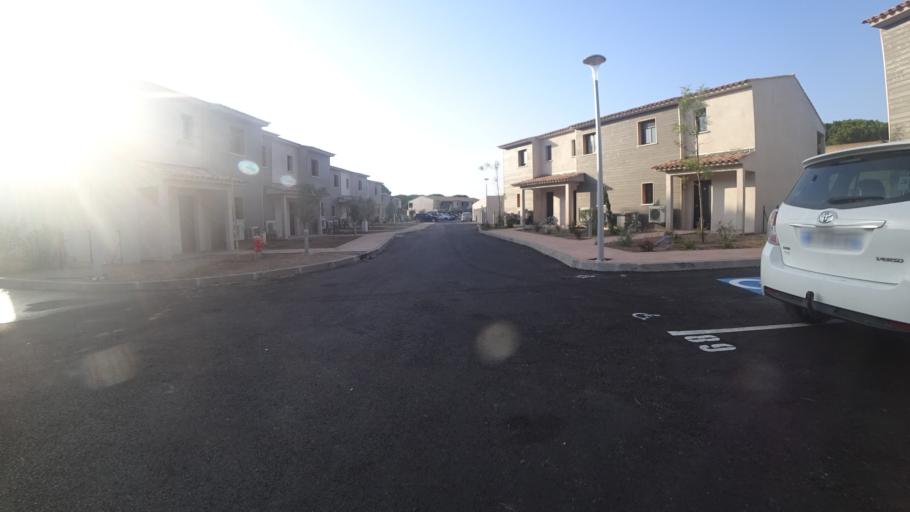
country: FR
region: Corsica
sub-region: Departement de la Corse-du-Sud
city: Porto-Vecchio
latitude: 41.6298
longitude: 9.3349
